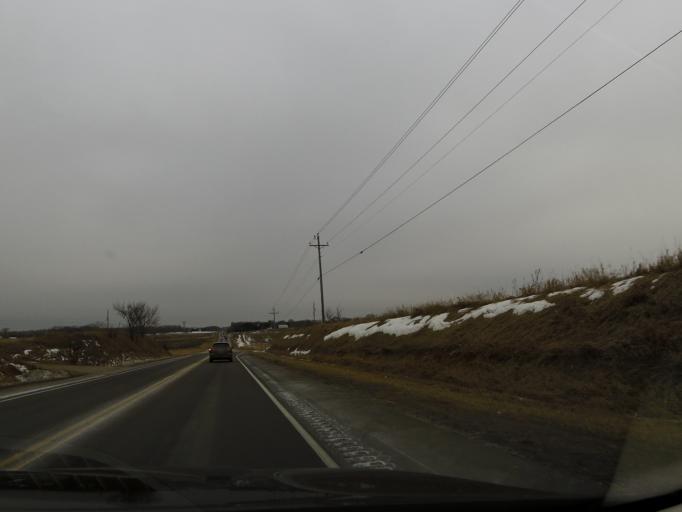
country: US
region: Minnesota
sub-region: Carver County
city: Young America (historical)
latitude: 44.7681
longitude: -93.8858
